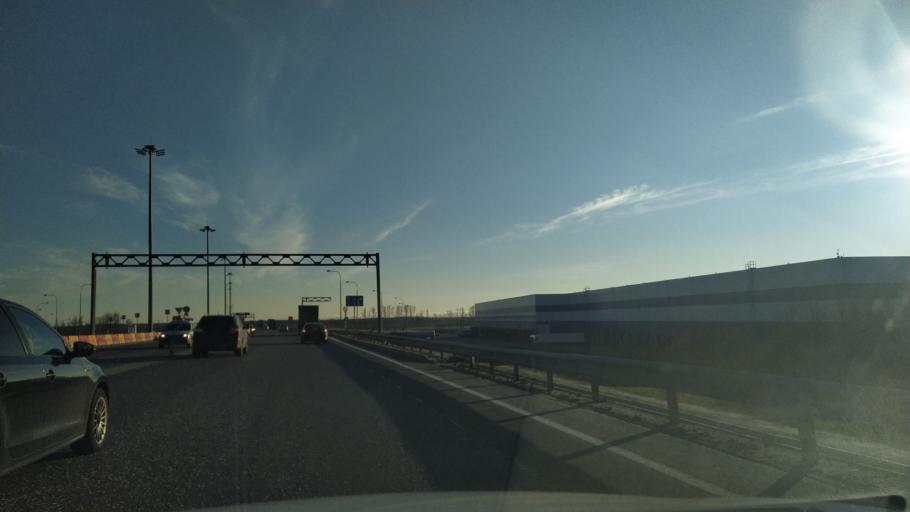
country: RU
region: St.-Petersburg
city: Pargolovo
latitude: 60.0947
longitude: 30.2519
